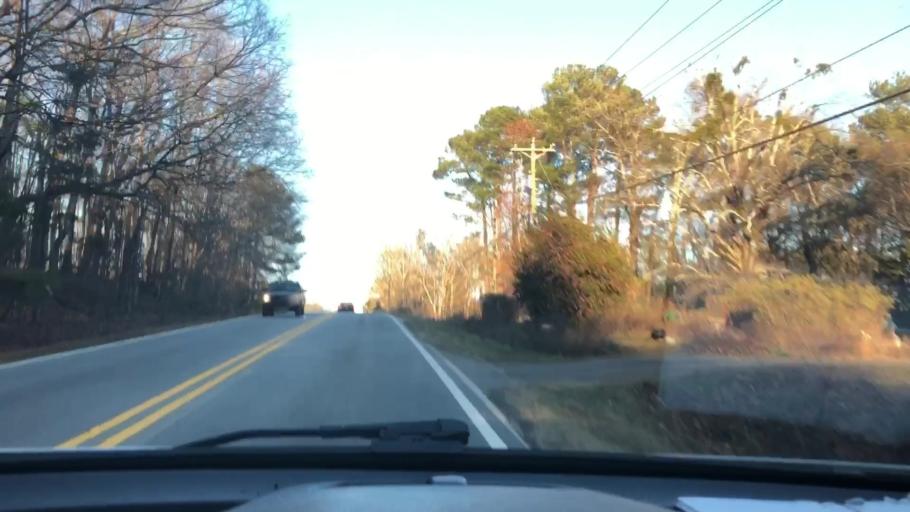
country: US
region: Georgia
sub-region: Rockdale County
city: Lakeview Estates
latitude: 33.7726
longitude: -83.9933
